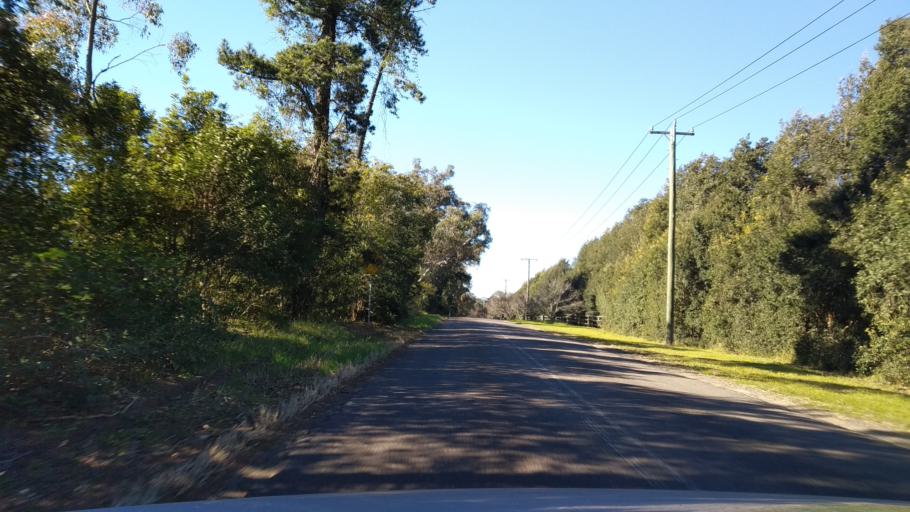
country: AU
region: New South Wales
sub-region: Wyong Shire
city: Little Jilliby
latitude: -33.2377
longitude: 151.2326
